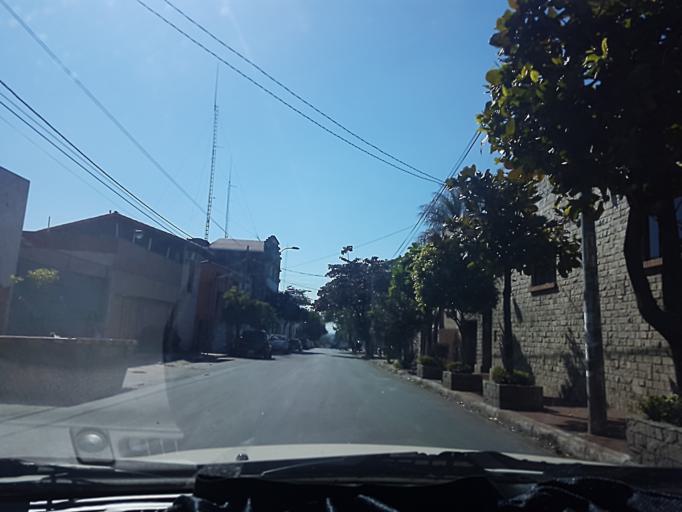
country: PY
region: Asuncion
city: Asuncion
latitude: -25.2836
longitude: -57.6466
